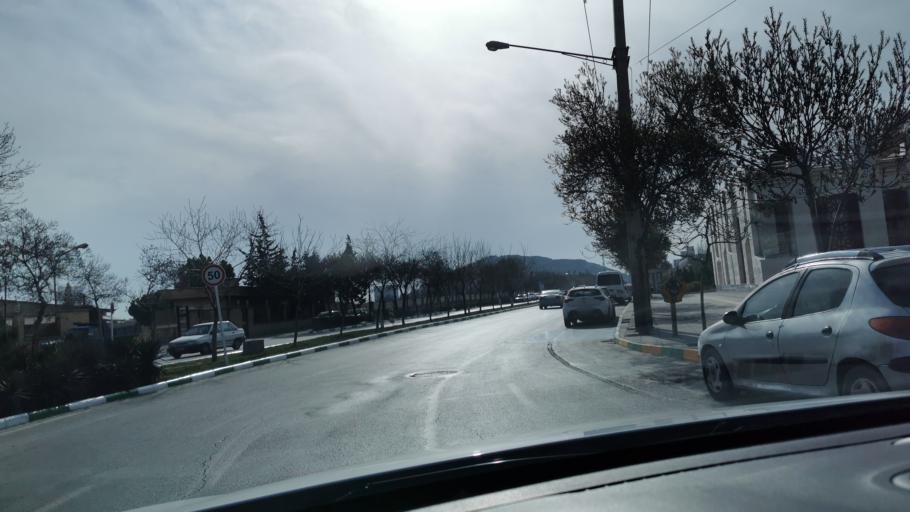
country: IR
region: Razavi Khorasan
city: Mashhad
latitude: 36.2840
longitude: 59.5492
